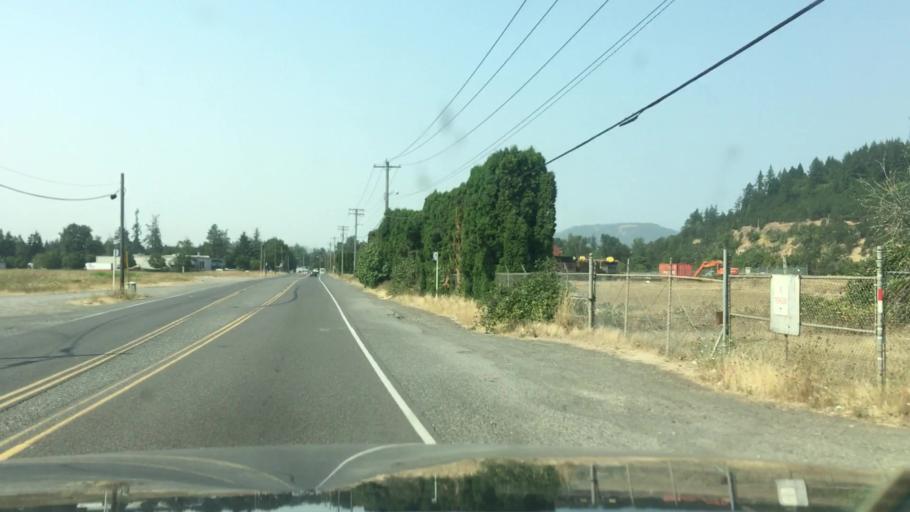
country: US
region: Oregon
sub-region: Lane County
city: Springfield
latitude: 44.0327
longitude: -123.0266
